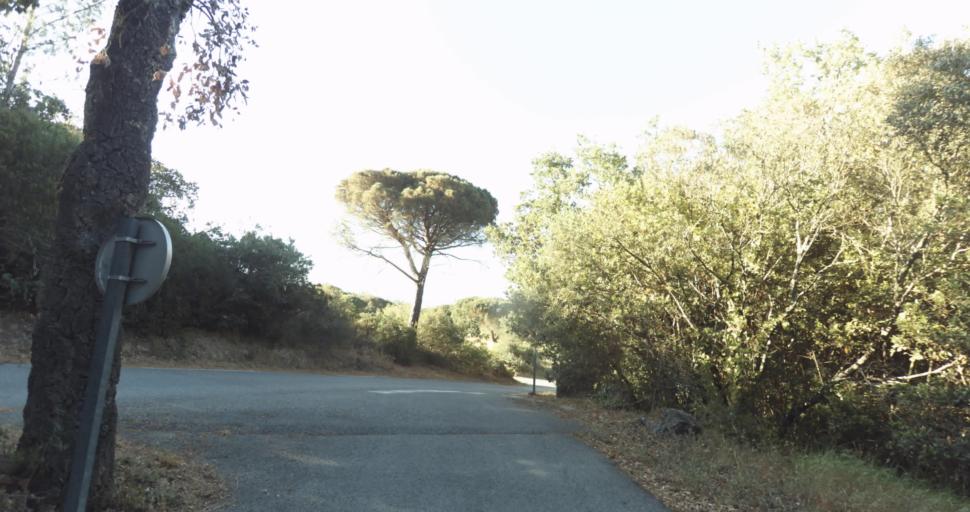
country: FR
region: Provence-Alpes-Cote d'Azur
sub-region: Departement du Var
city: Gassin
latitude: 43.2328
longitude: 6.5951
